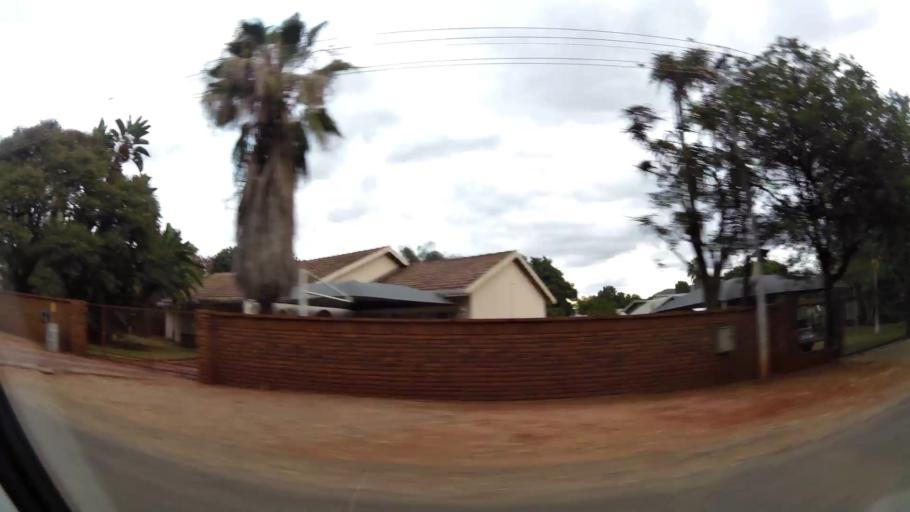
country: ZA
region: Limpopo
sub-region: Waterberg District Municipality
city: Mokopane
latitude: -24.1909
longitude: 28.9953
